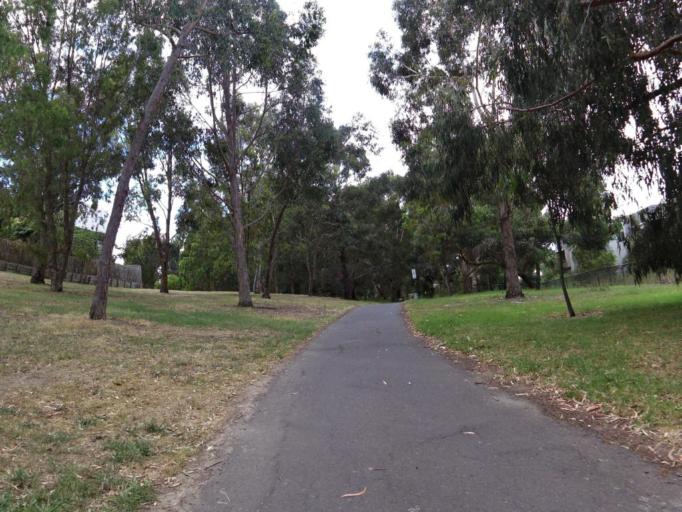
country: AU
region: Victoria
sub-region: Whitehorse
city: Burwood
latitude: -37.8535
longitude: 145.1087
